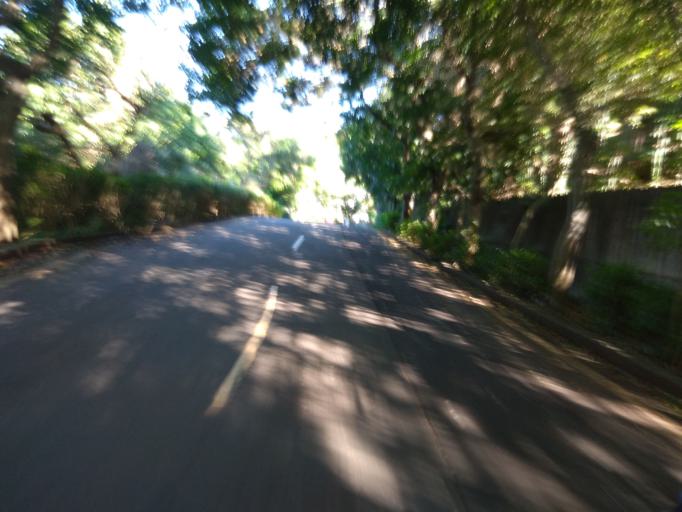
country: TW
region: Taiwan
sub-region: Hsinchu
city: Zhubei
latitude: 24.8508
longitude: 121.1070
